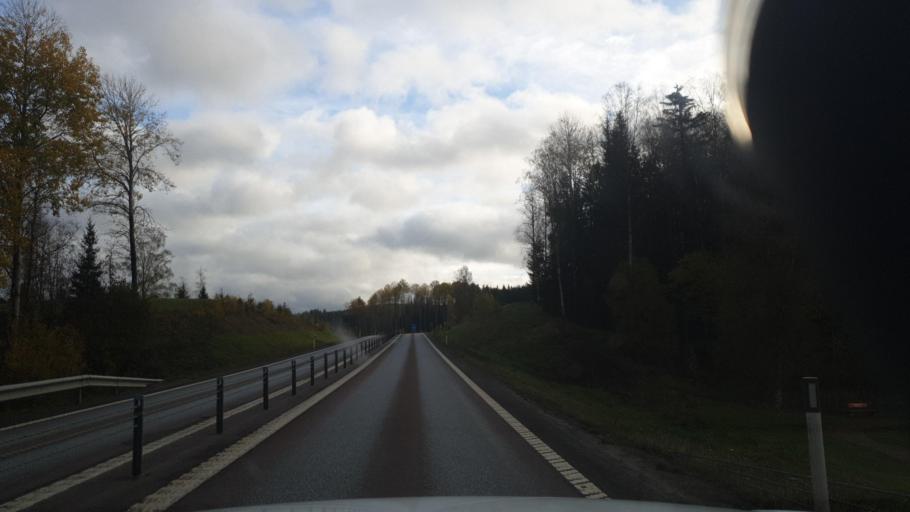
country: SE
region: Vaermland
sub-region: Arvika Kommun
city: Arvika
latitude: 59.6596
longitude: 12.7773
